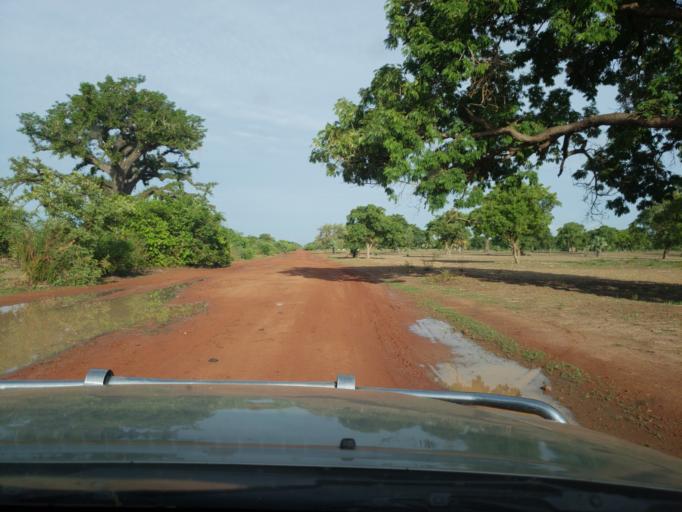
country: ML
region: Sikasso
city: Koutiala
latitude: 12.4184
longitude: -5.7063
